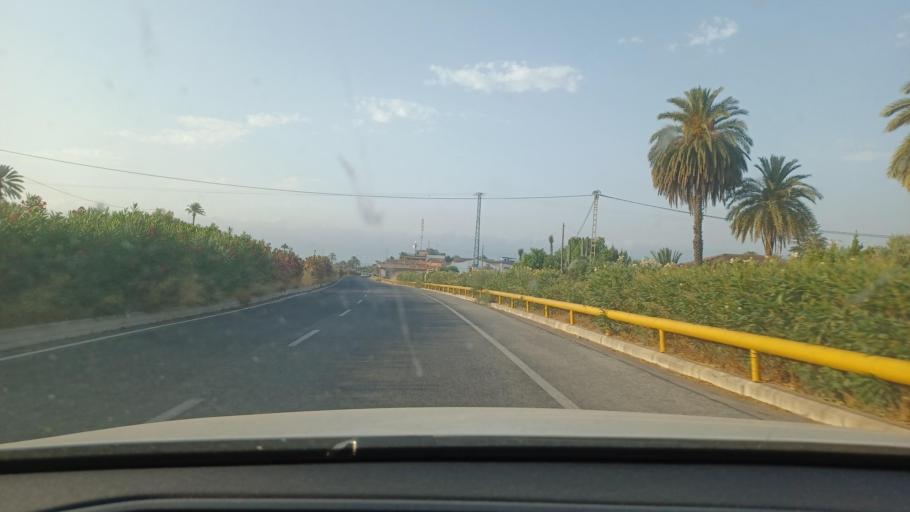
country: ES
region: Valencia
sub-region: Provincia de Alicante
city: Elche
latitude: 38.2277
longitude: -0.6991
